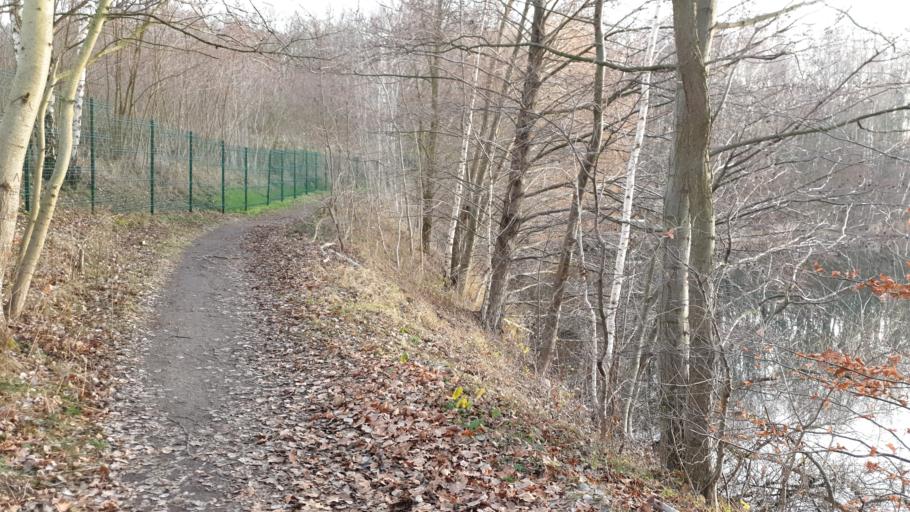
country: DE
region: Saxony
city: Hohburg
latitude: 51.4100
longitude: 12.7911
